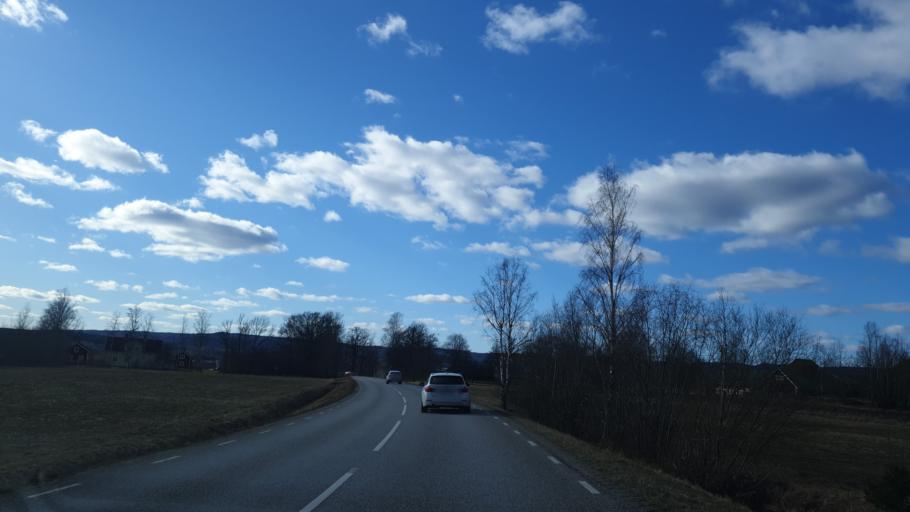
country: SE
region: OErebro
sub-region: Orebro Kommun
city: Garphyttan
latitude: 59.3379
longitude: 15.0677
